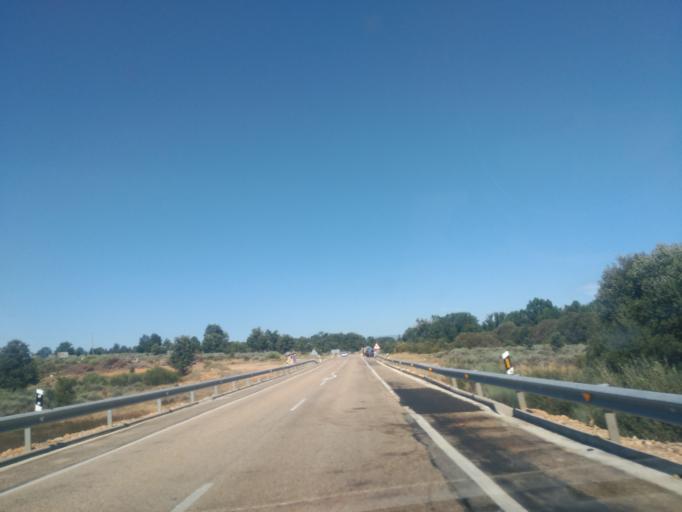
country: ES
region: Castille and Leon
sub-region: Provincia de Zamora
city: Otero de Bodas
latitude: 41.9501
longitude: -6.1991
